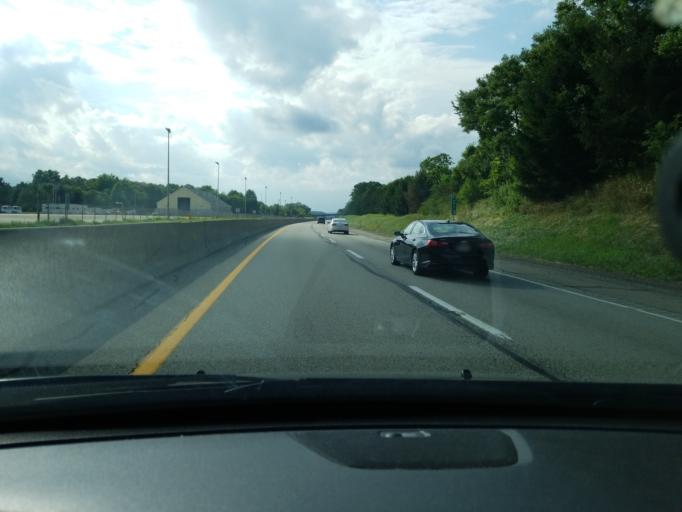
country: US
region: Pennsylvania
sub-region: Butler County
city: Zelienople
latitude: 40.7417
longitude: -80.1934
